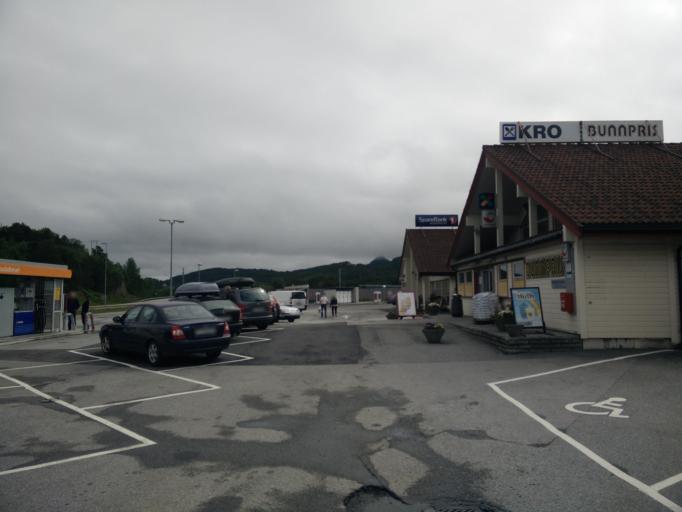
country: NO
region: More og Romsdal
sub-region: Kristiansund
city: Rensvik
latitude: 63.0112
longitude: 7.9762
